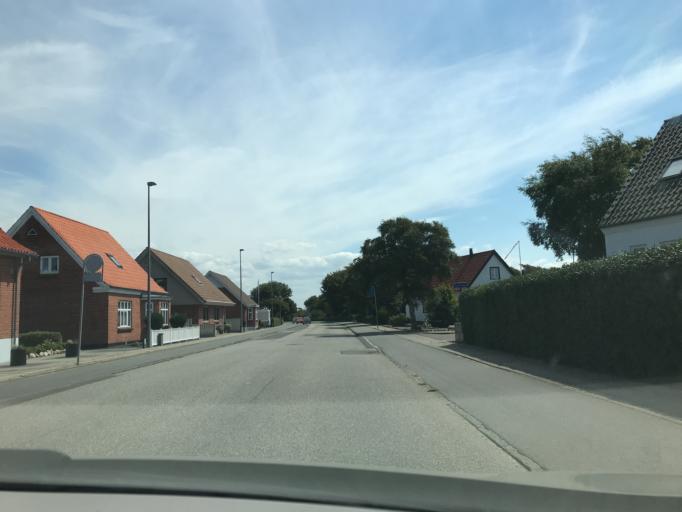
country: DK
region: Central Jutland
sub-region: Ringkobing-Skjern Kommune
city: Ringkobing
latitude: 56.0827
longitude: 8.2569
